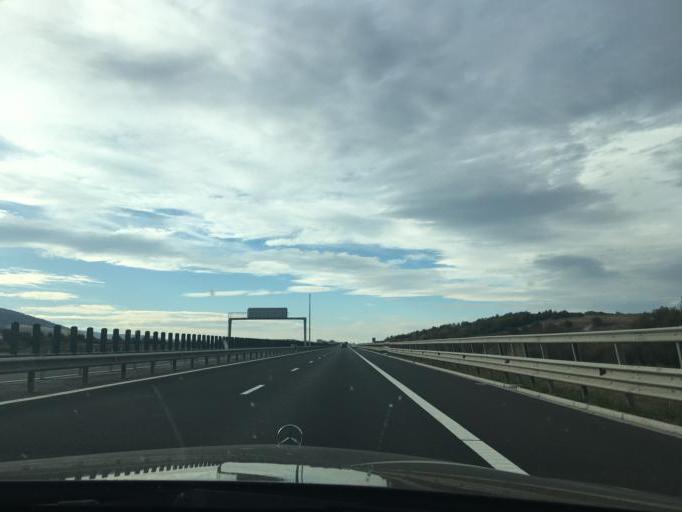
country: RO
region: Sibiu
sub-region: Oras Saliste
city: Saliste
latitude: 45.8110
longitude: 23.8975
